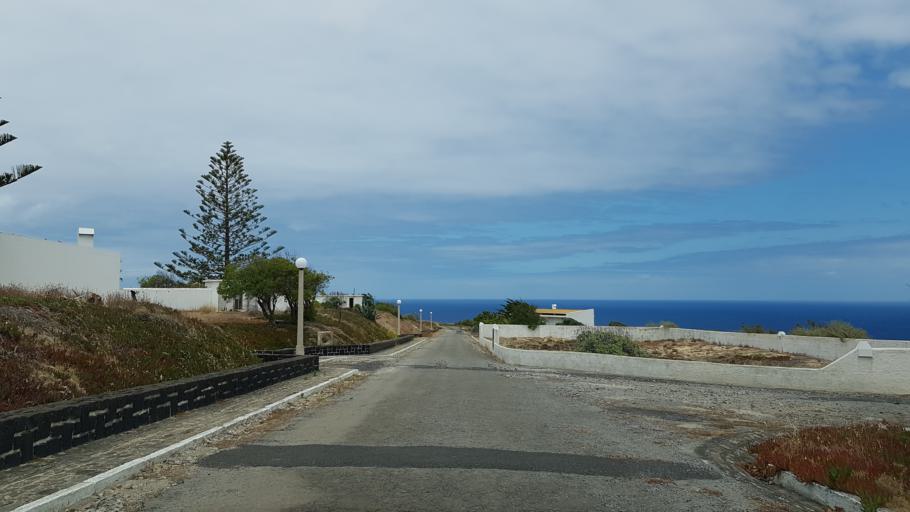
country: PT
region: Madeira
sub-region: Porto Santo
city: Camacha
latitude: 33.0875
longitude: -16.3392
